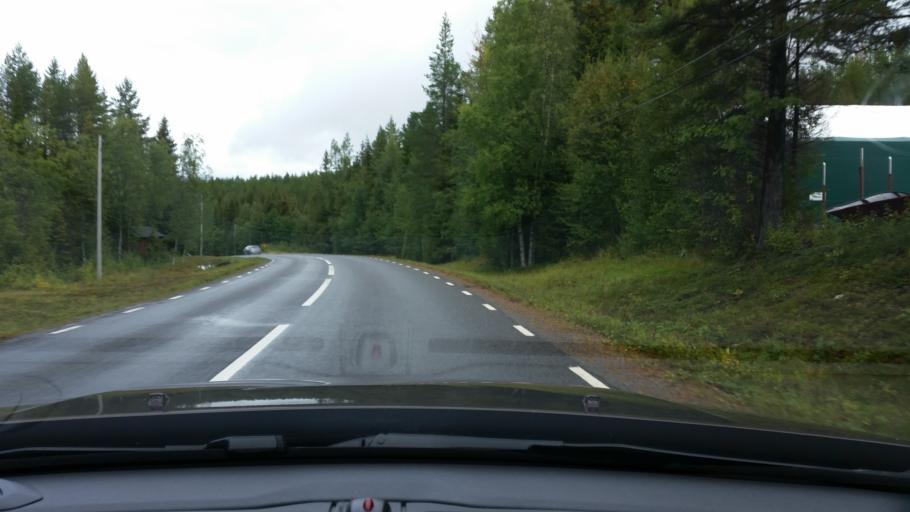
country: NO
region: Nord-Trondelag
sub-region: Lierne
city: Sandvika
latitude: 64.5081
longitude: 14.1577
